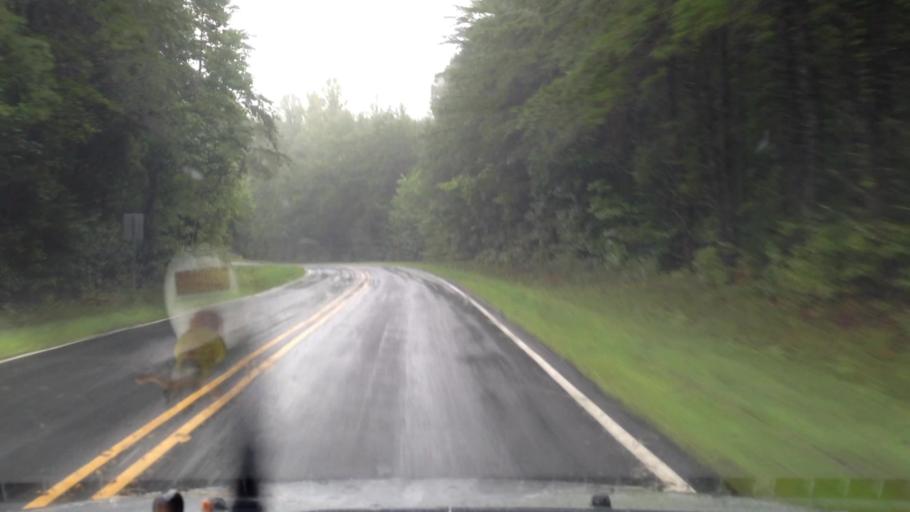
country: US
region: North Carolina
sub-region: Guilford County
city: Stokesdale
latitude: 36.2233
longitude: -80.0307
